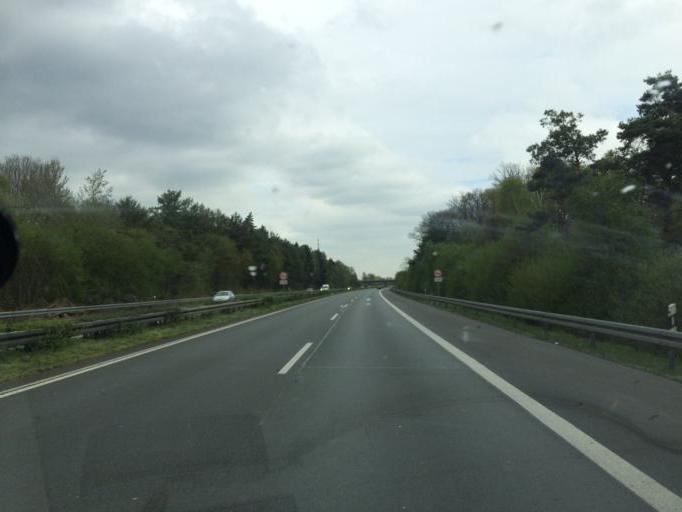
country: DE
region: North Rhine-Westphalia
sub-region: Regierungsbezirk Munster
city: Haltern
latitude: 51.8068
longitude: 7.1922
